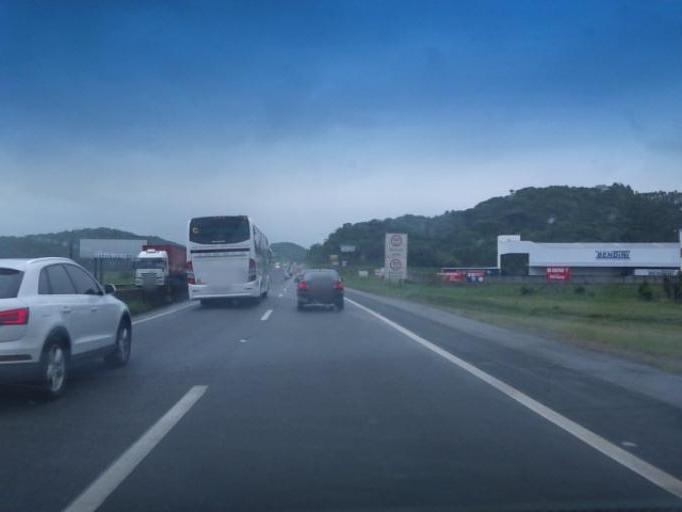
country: BR
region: Santa Catarina
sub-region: Penha
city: Penha
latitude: -26.8172
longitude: -48.6833
